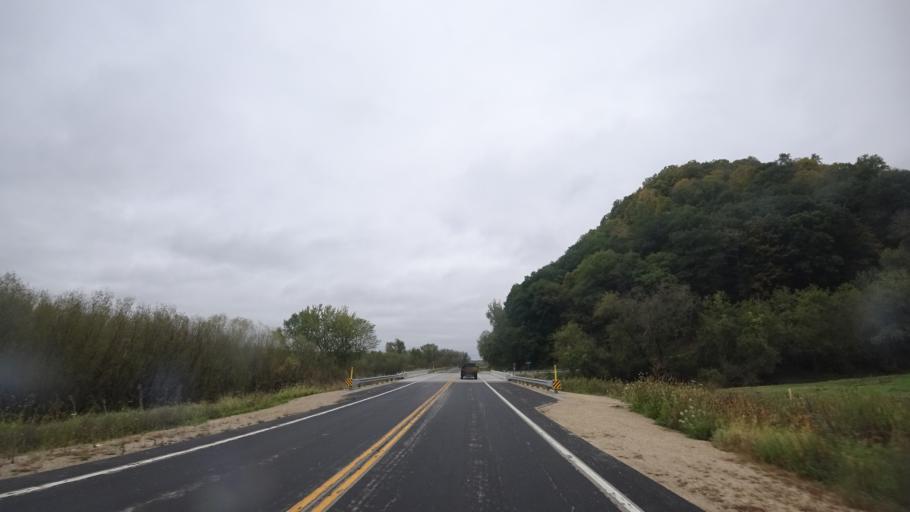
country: US
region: Wisconsin
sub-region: Grant County
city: Boscobel
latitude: 43.1259
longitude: -90.7704
